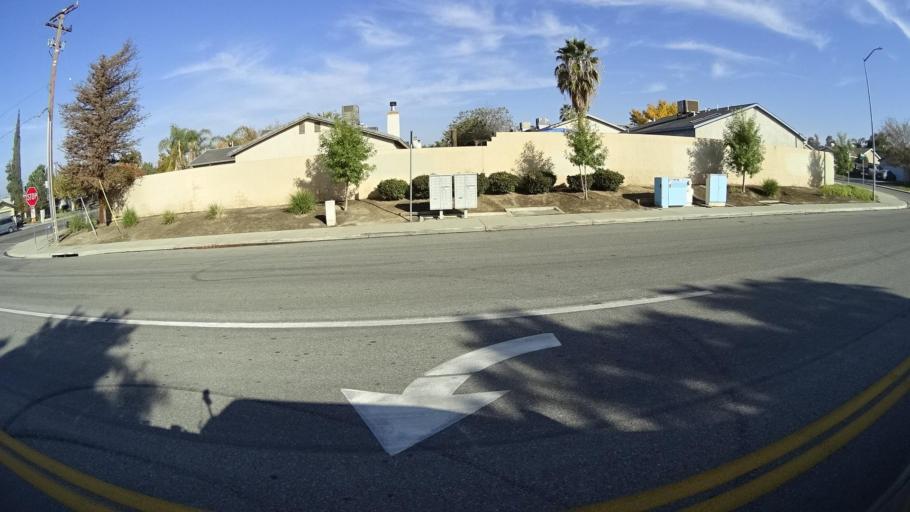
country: US
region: California
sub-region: Kern County
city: Lamont
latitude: 35.3690
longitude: -118.9048
